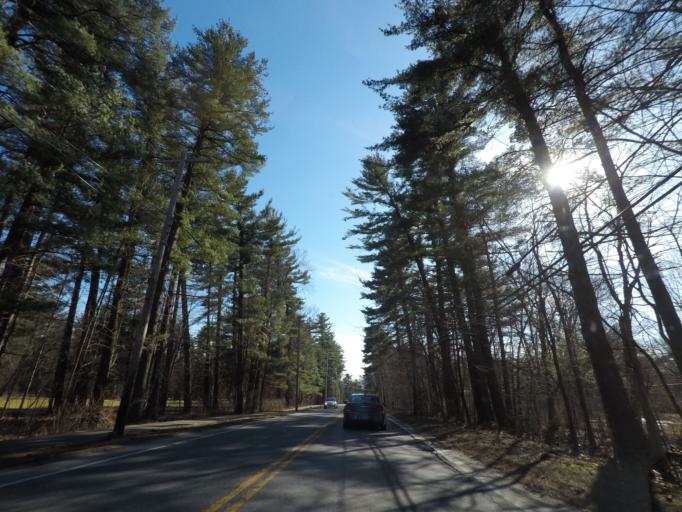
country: US
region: New York
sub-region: Saratoga County
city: Saratoga Springs
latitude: 43.0640
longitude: -73.7989
